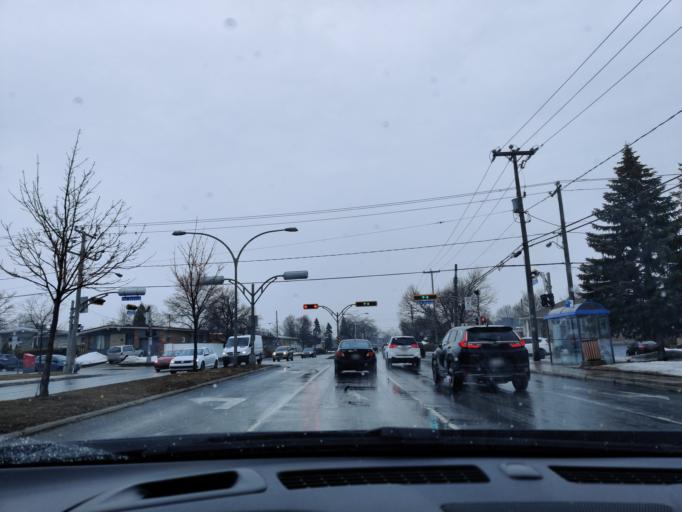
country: CA
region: Quebec
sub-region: Laval
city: Laval
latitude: 45.5327
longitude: -73.7515
